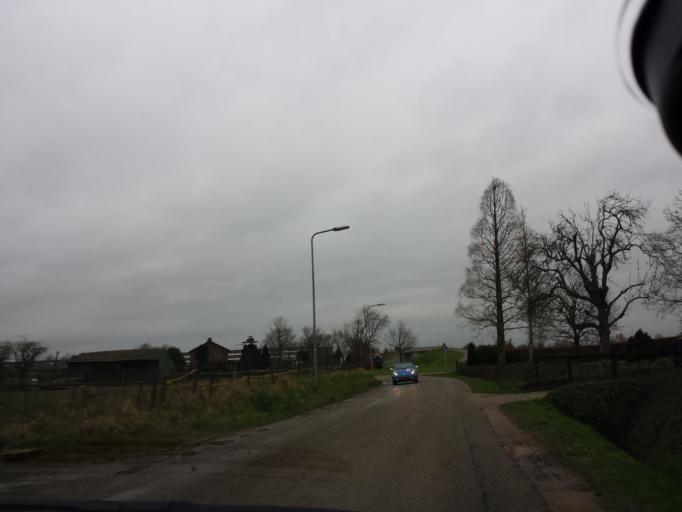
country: NL
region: Limburg
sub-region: Gemeente Roerdalen
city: Melick
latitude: 51.1867
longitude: 6.0320
